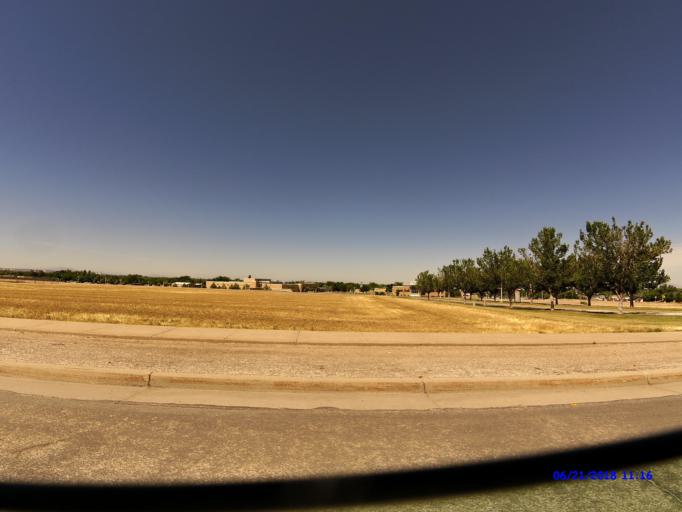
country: US
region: Utah
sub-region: Weber County
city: Harrisville
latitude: 41.2649
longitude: -111.9592
